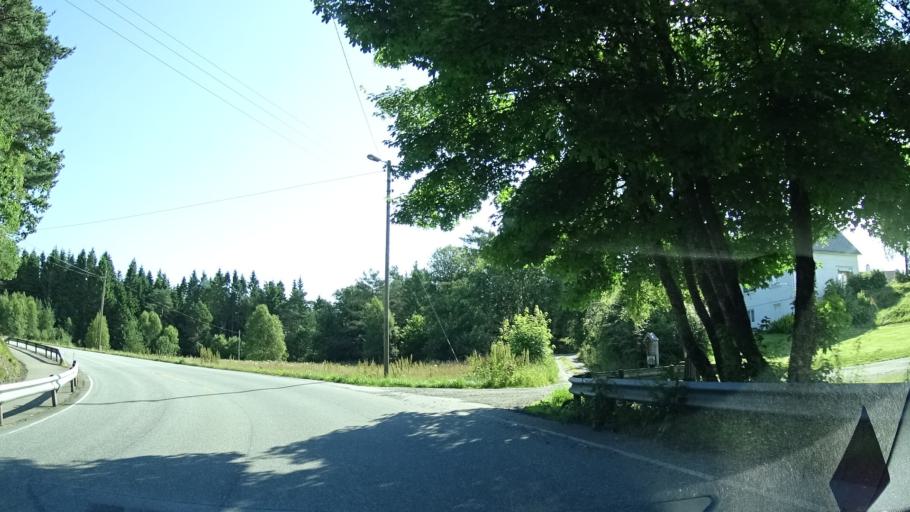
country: NO
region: Hordaland
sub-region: Stord
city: Sagvag
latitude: 59.7680
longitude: 5.4327
